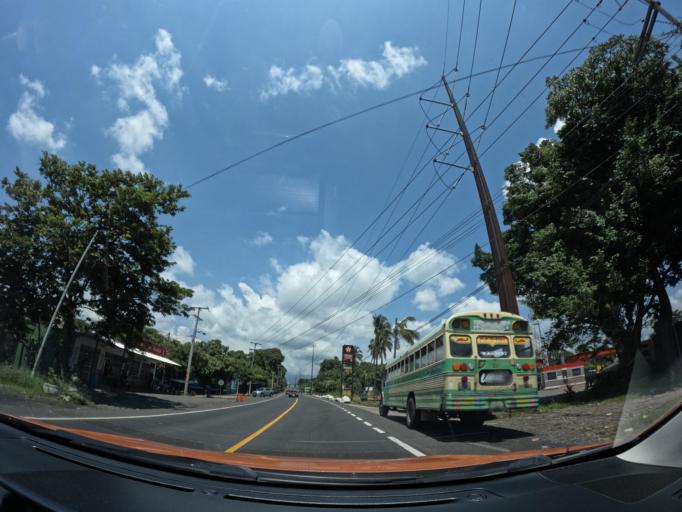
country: GT
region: Escuintla
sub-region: Municipio de Escuintla
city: Escuintla
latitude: 14.2694
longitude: -90.7927
